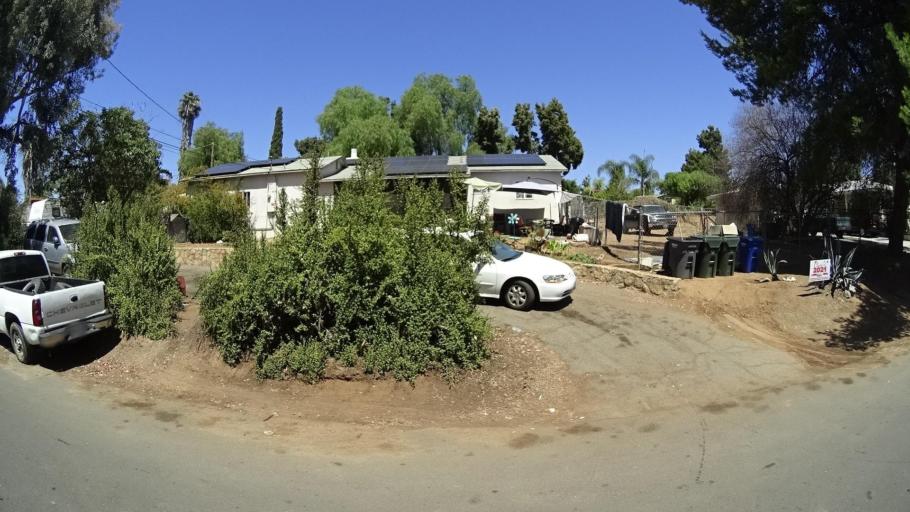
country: US
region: California
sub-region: San Diego County
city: Fallbrook
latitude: 33.3864
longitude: -117.2492
